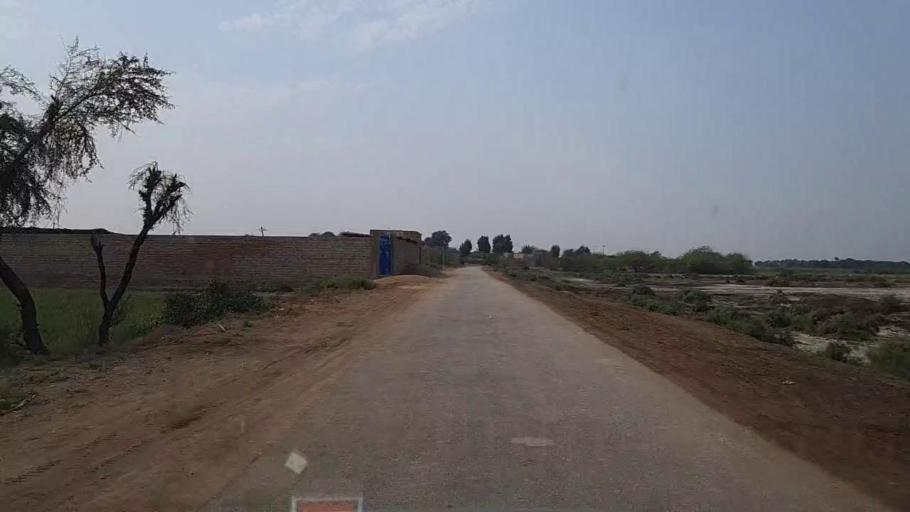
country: PK
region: Sindh
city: Mirwah Gorchani
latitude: 25.3283
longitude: 69.0370
